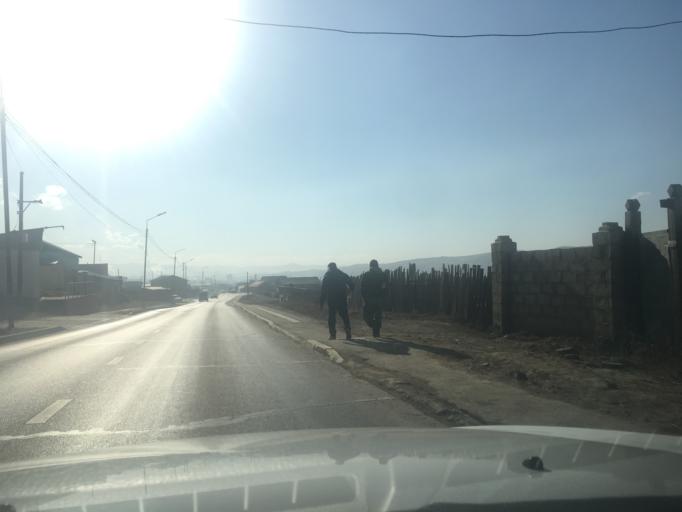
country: MN
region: Ulaanbaatar
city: Ulaanbaatar
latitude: 47.9624
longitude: 106.8281
